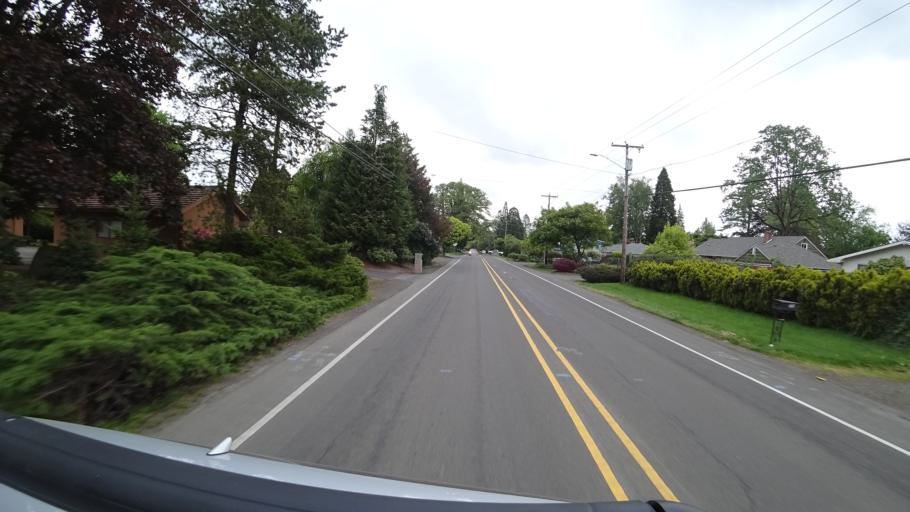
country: US
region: Oregon
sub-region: Washington County
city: Hillsboro
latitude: 45.5300
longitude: -122.9817
